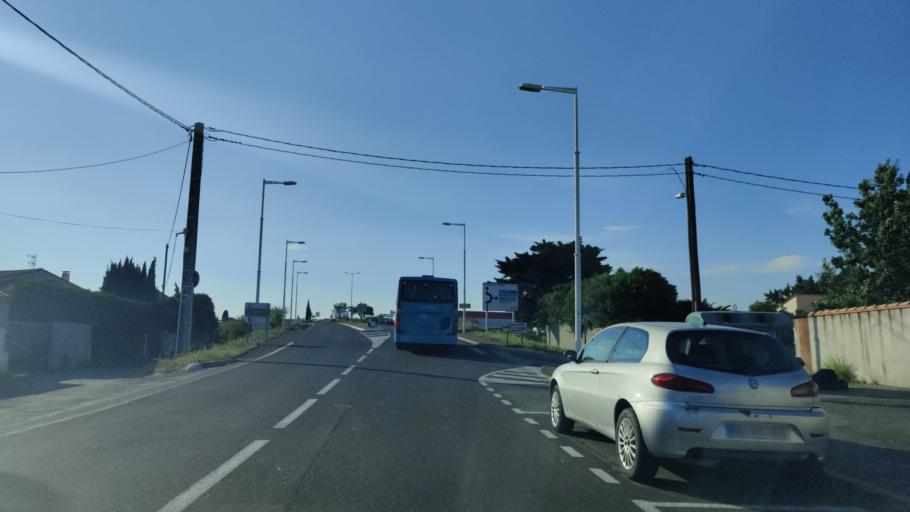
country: FR
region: Languedoc-Roussillon
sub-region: Departement des Pyrenees-Orientales
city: Perpignan
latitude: 42.7257
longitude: 2.8809
